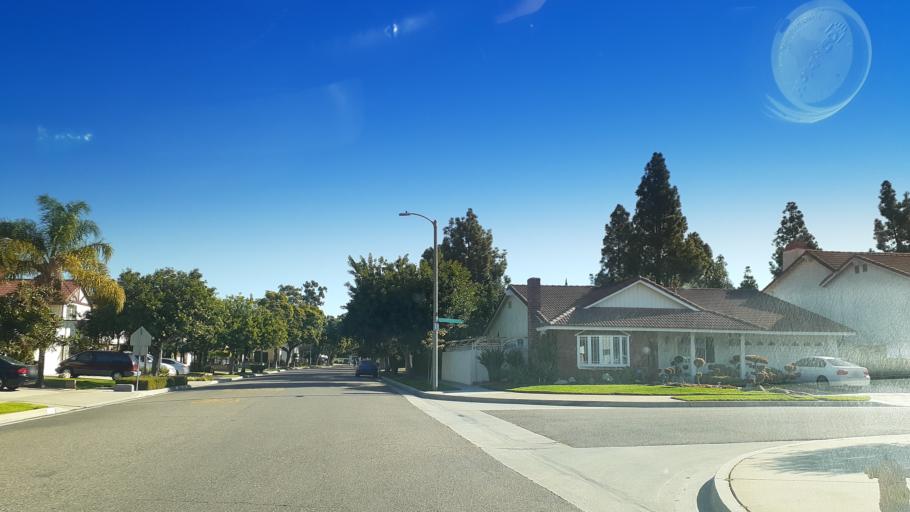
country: US
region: California
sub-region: Los Angeles County
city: Cerritos
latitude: 33.8619
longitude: -118.0672
